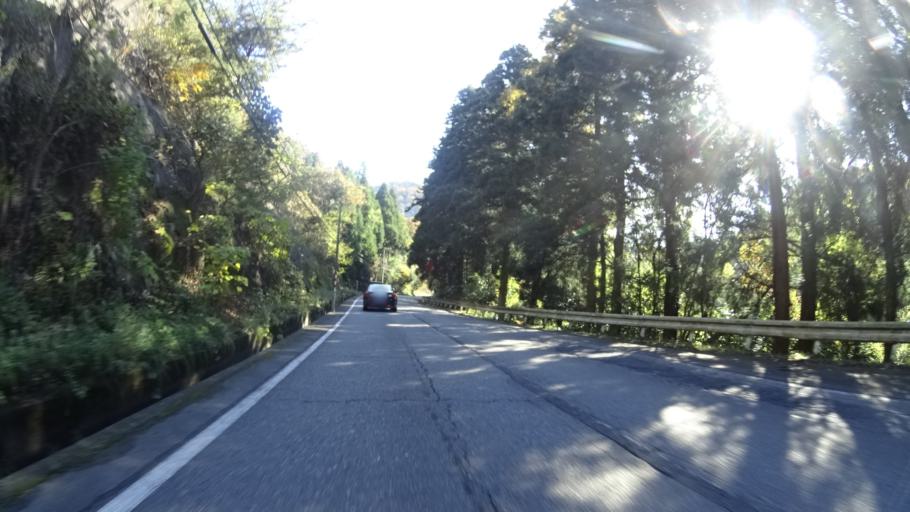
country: JP
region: Ishikawa
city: Komatsu
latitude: 36.3781
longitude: 136.5390
